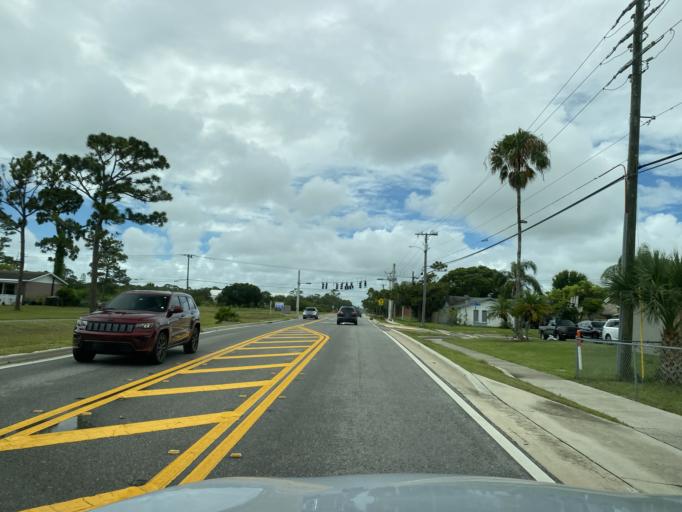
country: US
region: Florida
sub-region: Brevard County
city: West Melbourne
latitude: 28.0654
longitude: -80.6537
